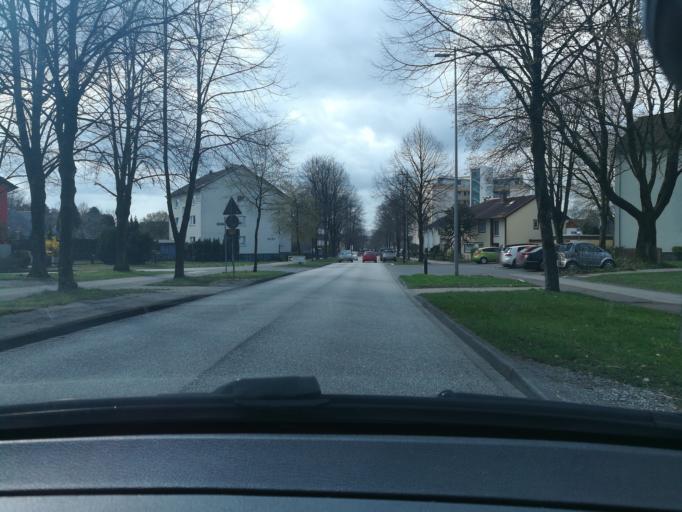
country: DE
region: North Rhine-Westphalia
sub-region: Regierungsbezirk Detmold
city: Oerlinghausen
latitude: 51.9519
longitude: 8.5838
